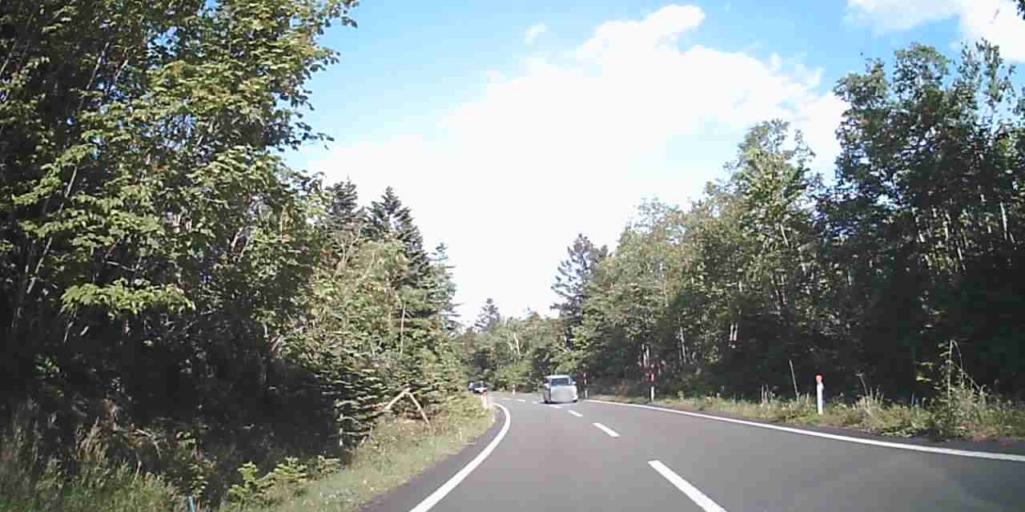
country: JP
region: Hokkaido
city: Shiraoi
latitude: 42.6885
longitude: 141.4307
